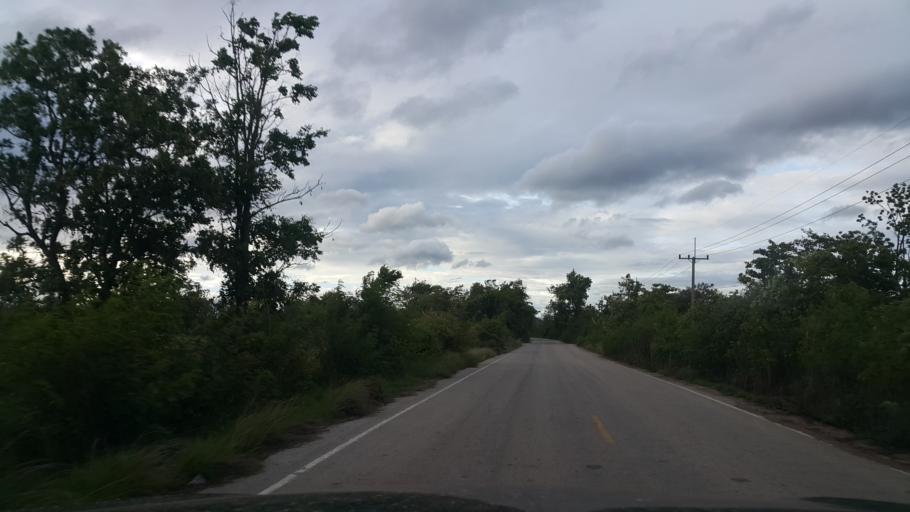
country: TH
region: Sukhothai
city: Thung Saliam
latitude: 17.1694
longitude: 99.5243
